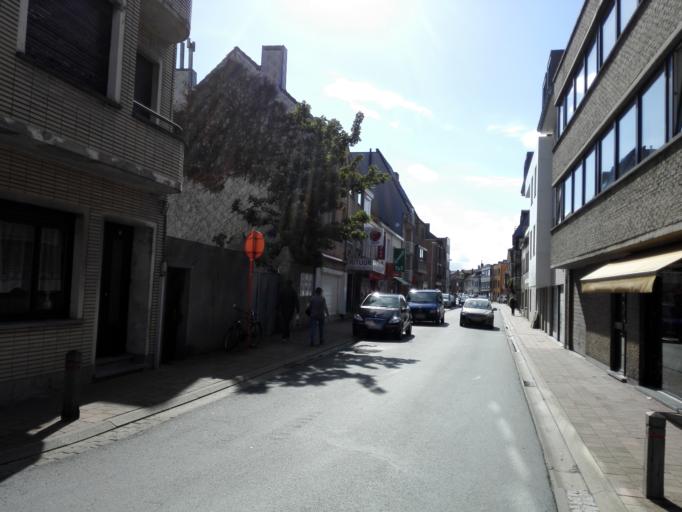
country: BE
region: Flanders
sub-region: Provincie West-Vlaanderen
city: Bredene
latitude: 51.2461
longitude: 2.9627
